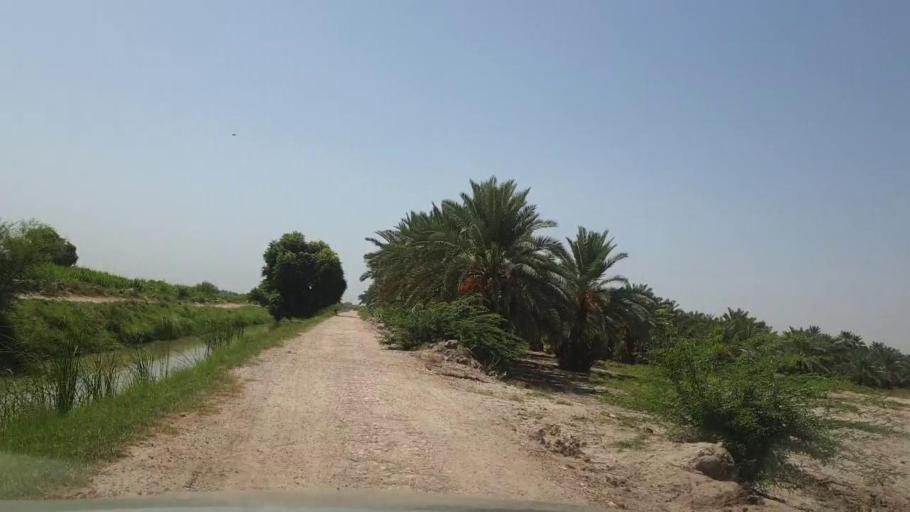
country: PK
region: Sindh
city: Rohri
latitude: 27.6648
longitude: 68.9805
